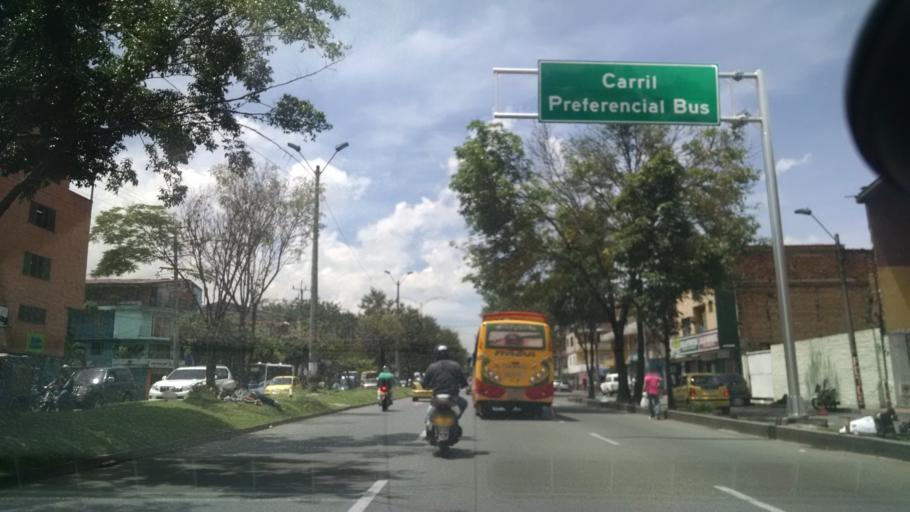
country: CO
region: Antioquia
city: Itagui
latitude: 6.2066
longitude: -75.5862
